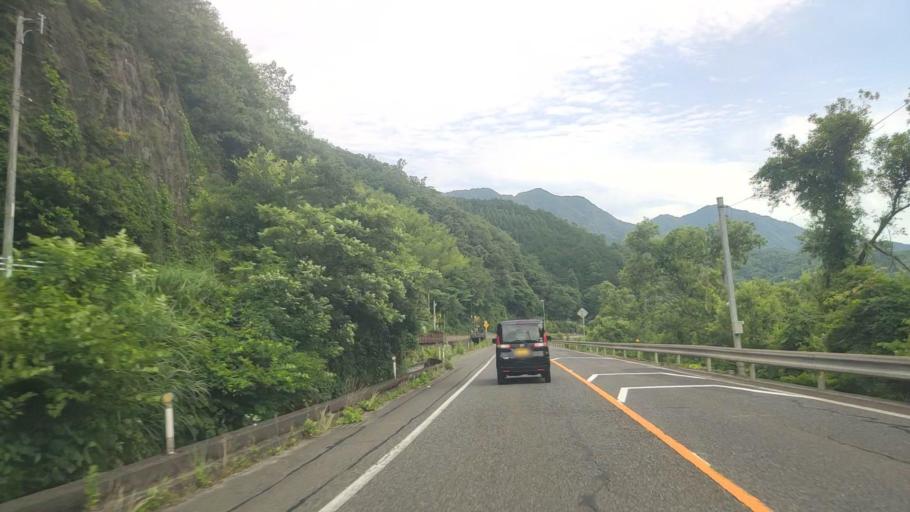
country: JP
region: Tottori
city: Tottori
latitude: 35.3499
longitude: 134.2045
